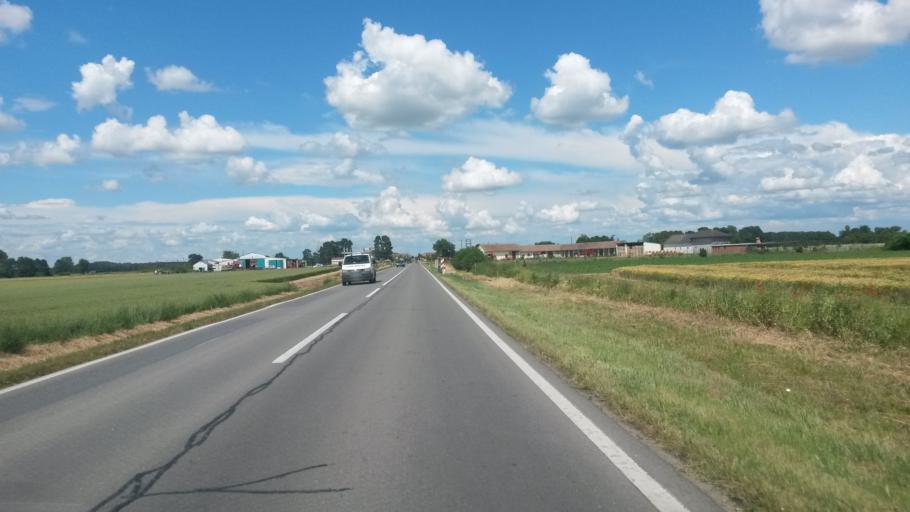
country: HR
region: Osjecko-Baranjska
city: Viskovci
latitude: 45.3964
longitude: 18.4584
